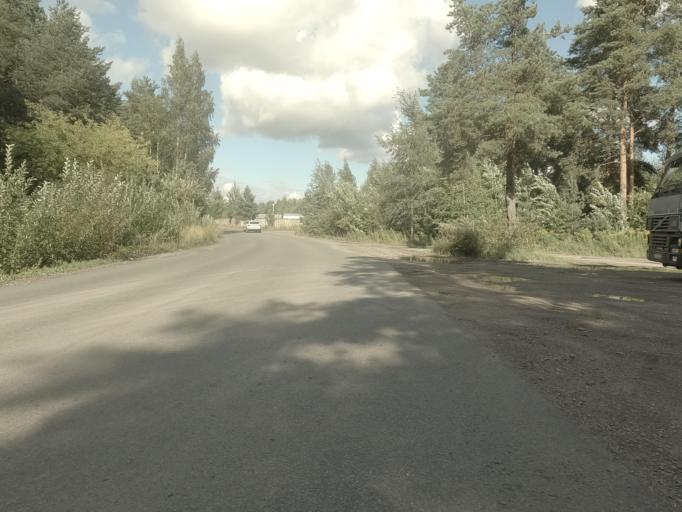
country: RU
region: Leningrad
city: Vsevolozhsk
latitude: 60.0037
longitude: 30.6416
